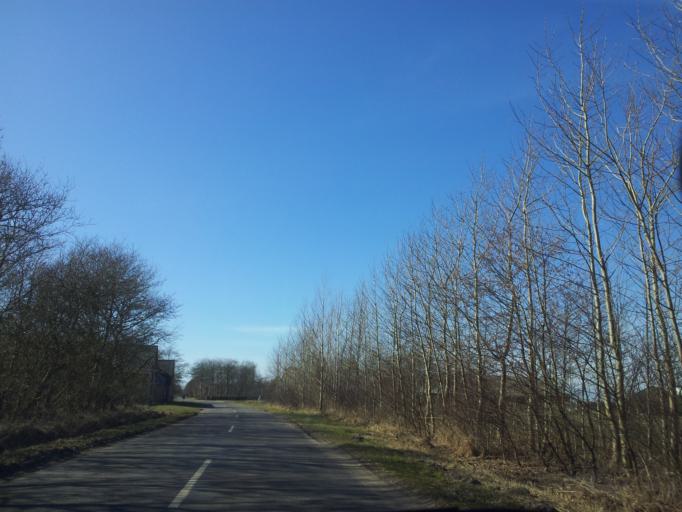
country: DK
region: South Denmark
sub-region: Tonder Kommune
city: Sherrebek
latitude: 55.1734
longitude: 8.7247
